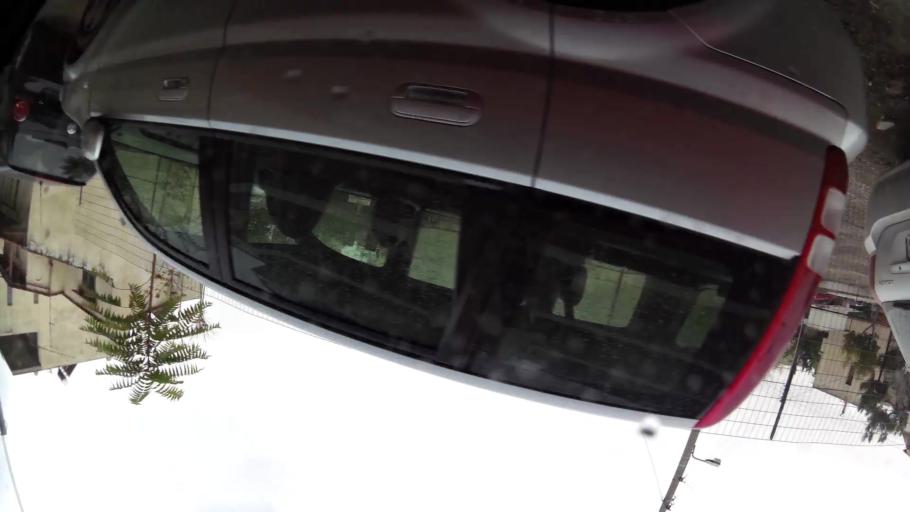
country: GR
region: Attica
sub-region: Nomarchia Athinas
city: Nea Filadelfeia
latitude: 38.0377
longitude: 23.7295
